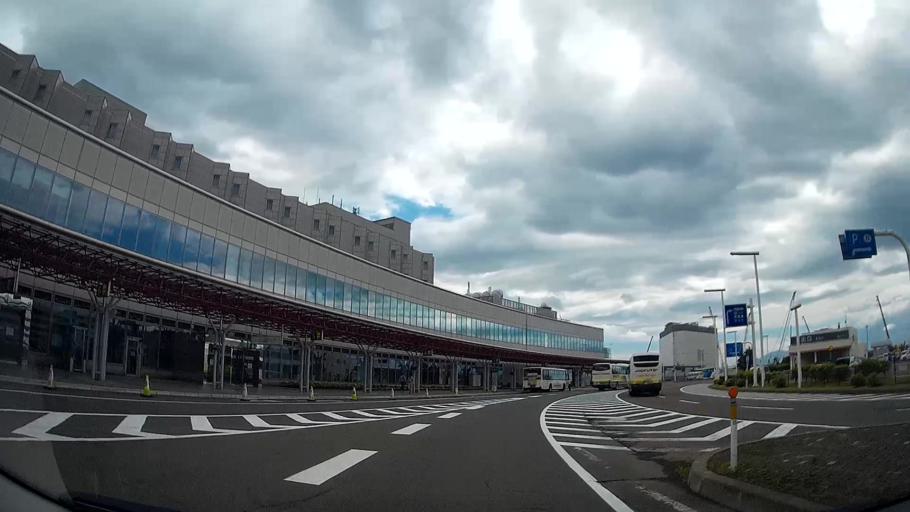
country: JP
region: Hokkaido
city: Chitose
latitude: 42.7861
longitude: 141.6805
